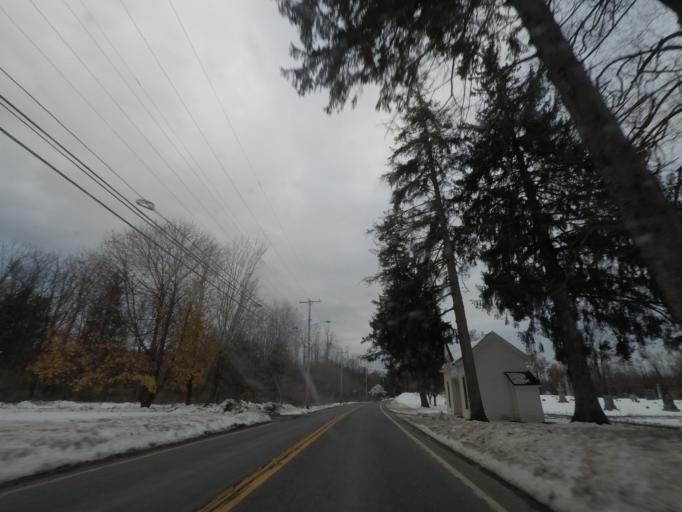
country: US
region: New York
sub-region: Ulster County
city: Clintondale
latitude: 41.6738
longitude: -74.1038
